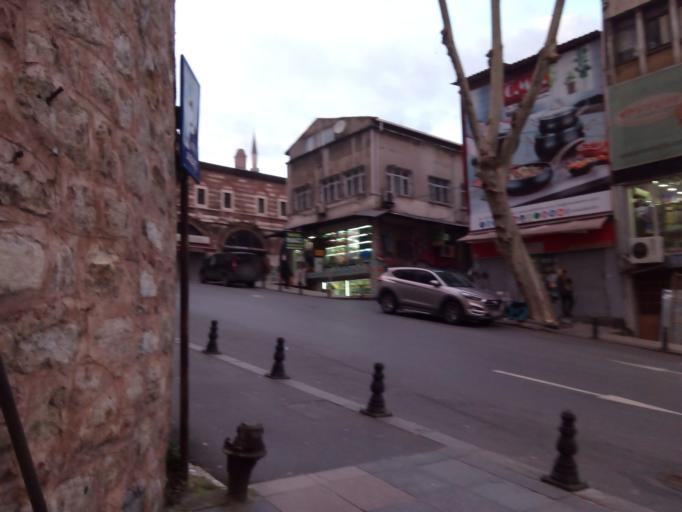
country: TR
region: Istanbul
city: Eminoenue
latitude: 41.0148
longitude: 28.9659
